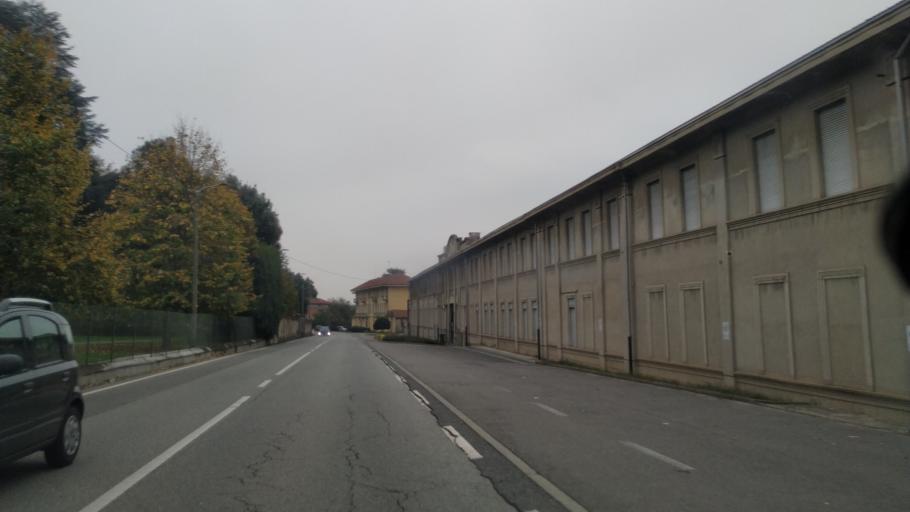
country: IT
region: Piedmont
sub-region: Provincia di Biella
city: Cossato
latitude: 45.5737
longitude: 8.1863
